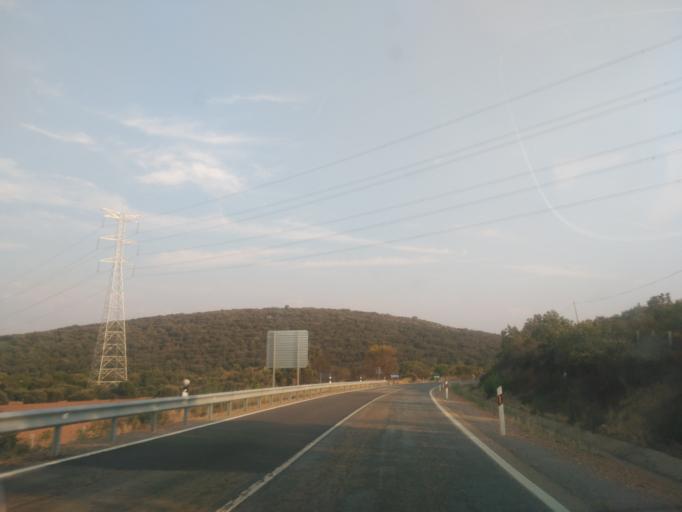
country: ES
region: Castille and Leon
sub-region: Provincia de Zamora
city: Perilla de Castro
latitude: 41.7562
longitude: -5.8556
